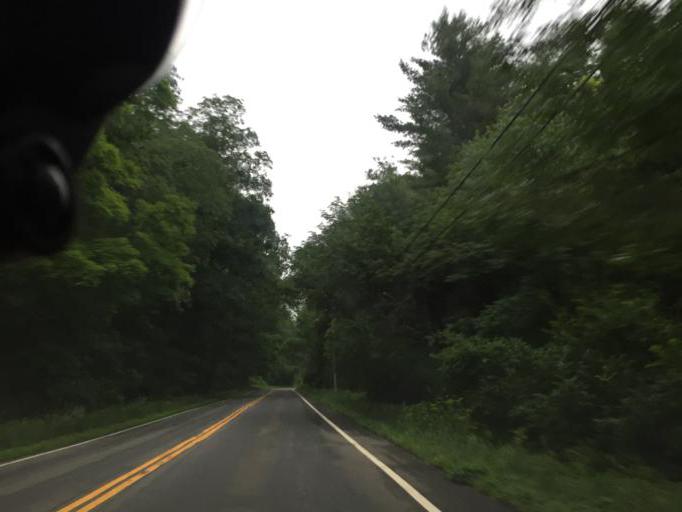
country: US
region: Connecticut
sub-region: Litchfield County
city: Canaan
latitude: 41.9322
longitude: -73.2898
